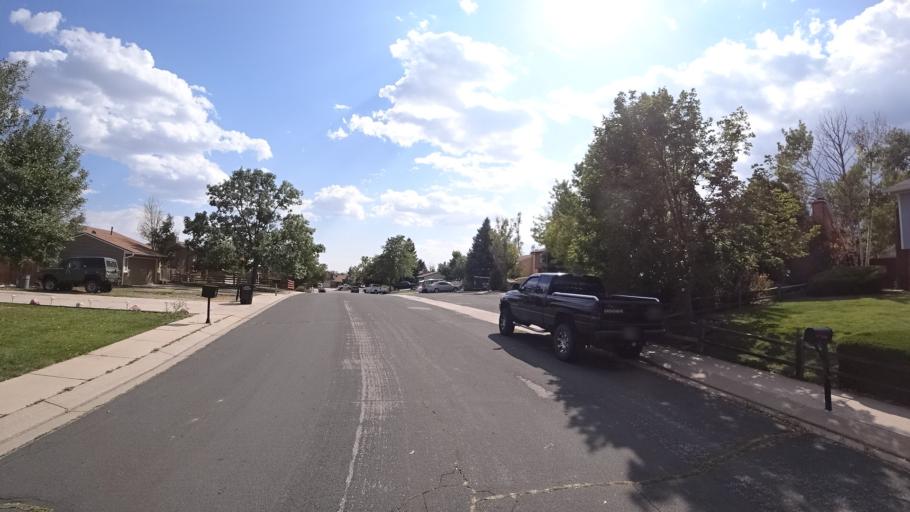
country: US
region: Colorado
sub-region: El Paso County
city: Cimarron Hills
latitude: 38.8746
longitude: -104.7246
